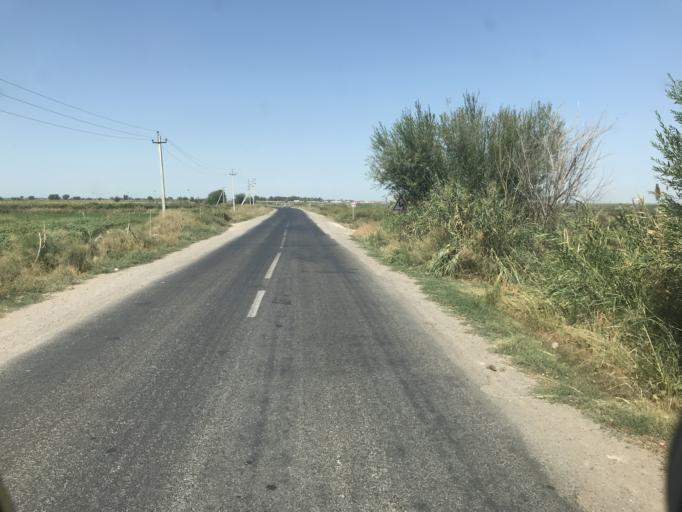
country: KZ
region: Ongtustik Qazaqstan
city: Ilyich
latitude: 40.9503
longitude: 68.4834
